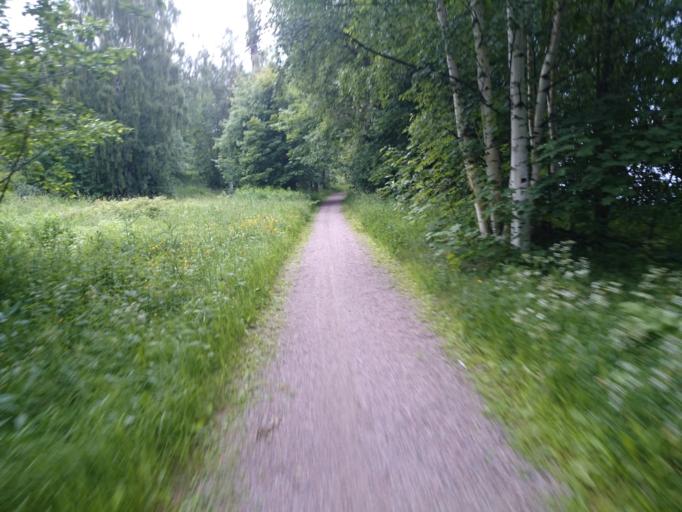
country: SE
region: Vaesternorrland
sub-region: Sundsvalls Kommun
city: Kvissleby
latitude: 62.3048
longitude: 17.3758
